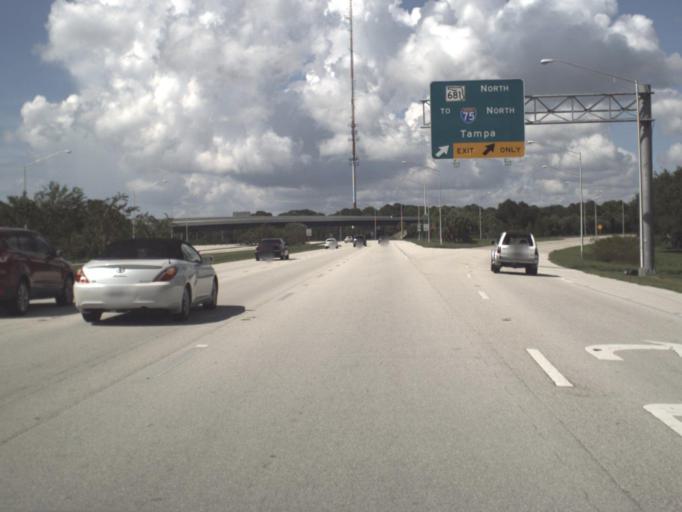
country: US
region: Florida
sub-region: Sarasota County
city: Laurel
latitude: 27.1465
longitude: -82.4624
